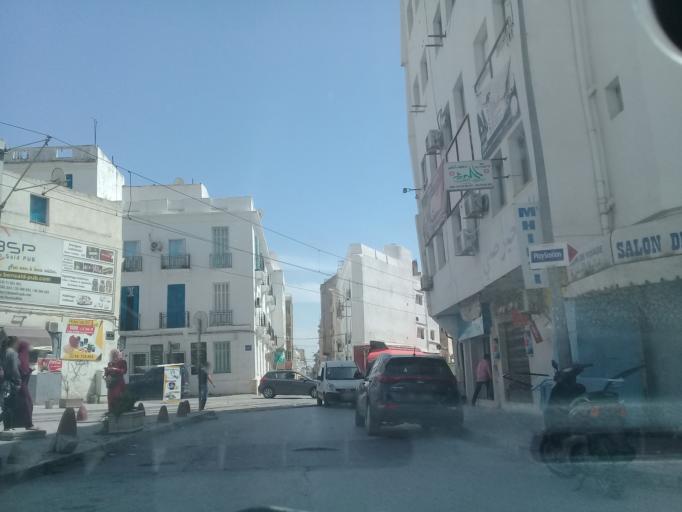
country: TN
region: Tunis
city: Tunis
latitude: 36.8120
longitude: 10.1827
